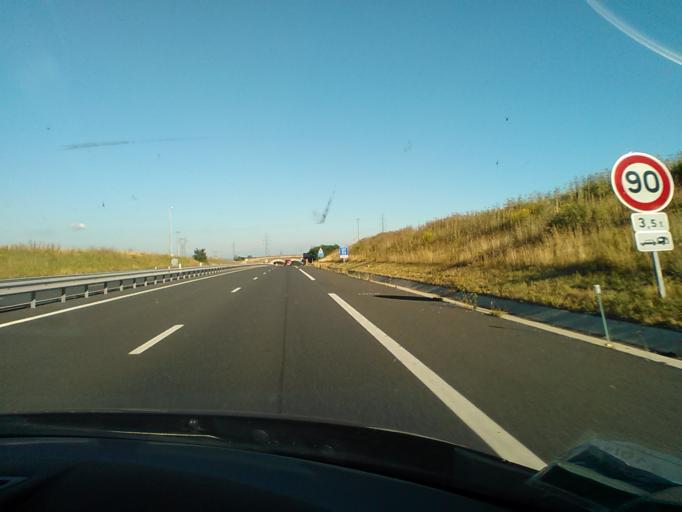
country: FR
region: Rhone-Alpes
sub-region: Departement de l'Ain
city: Beynost
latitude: 45.8539
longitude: 5.0010
